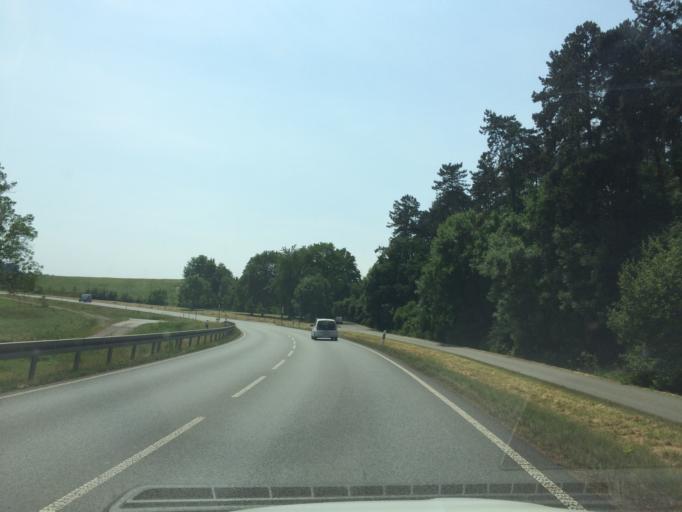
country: DE
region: Hesse
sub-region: Regierungsbezirk Kassel
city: Hofgeismar
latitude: 51.4778
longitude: 9.3908
